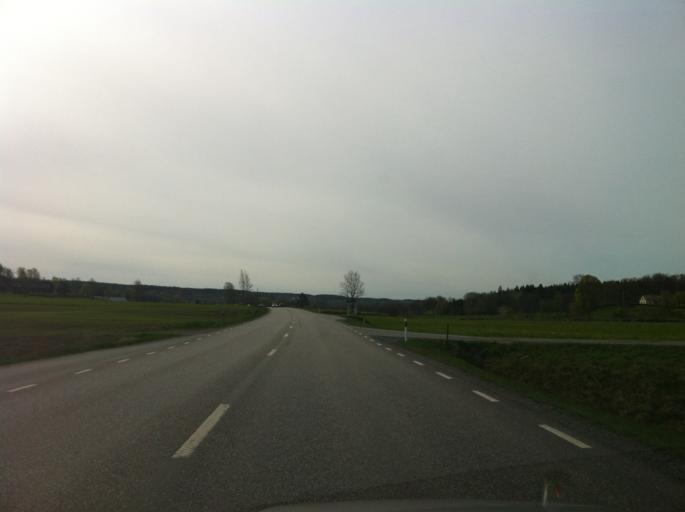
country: SE
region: Vaestra Goetaland
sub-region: Harryda Kommun
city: Ravlanda
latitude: 57.5335
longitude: 12.5327
